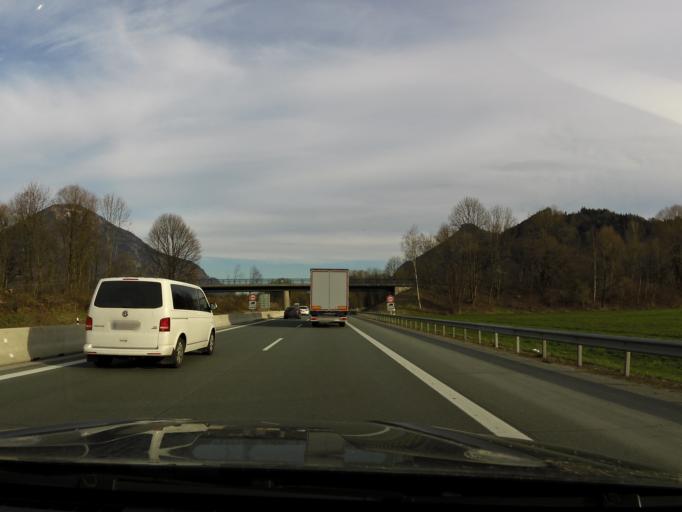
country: DE
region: Bavaria
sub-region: Upper Bavaria
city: Oberaudorf
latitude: 47.6507
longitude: 12.1875
